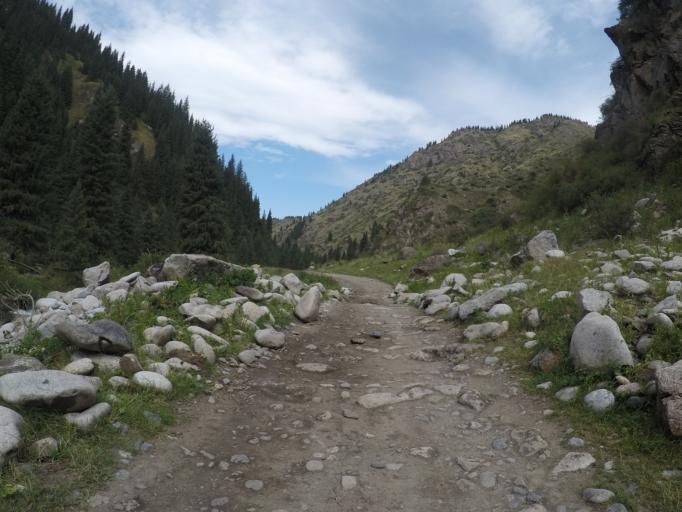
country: KG
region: Ysyk-Koel
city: Teploklyuchenka
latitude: 42.4386
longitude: 78.5590
